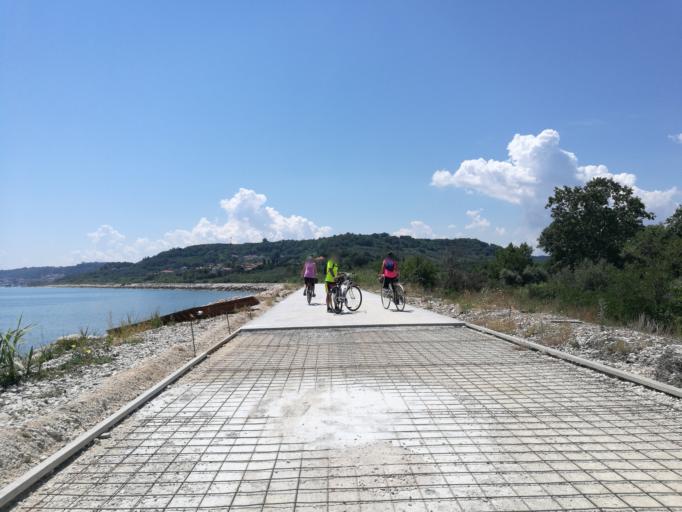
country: IT
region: Abruzzo
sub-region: Provincia di Chieti
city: Marina di San Vito
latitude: 42.3296
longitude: 14.4245
